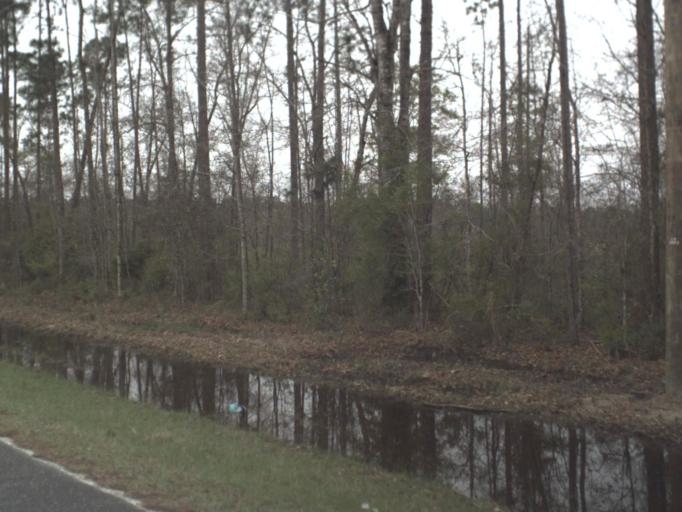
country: US
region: Florida
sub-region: Gulf County
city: Wewahitchka
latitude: 30.0102
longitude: -84.9786
